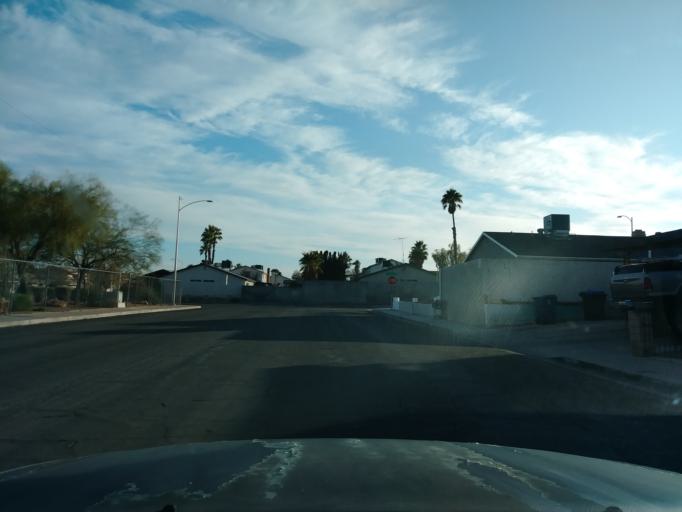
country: US
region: Nevada
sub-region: Clark County
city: Spring Valley
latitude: 36.1688
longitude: -115.2354
